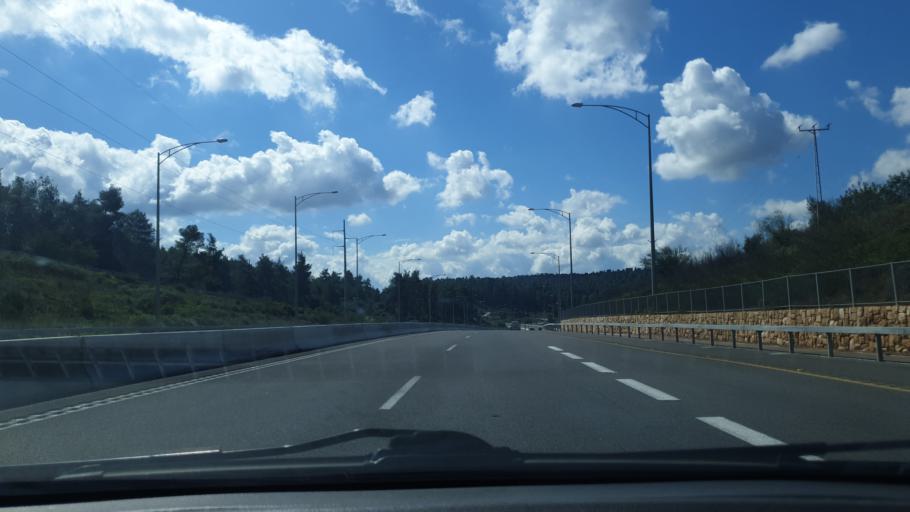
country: IL
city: Mevo horon
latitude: 31.8049
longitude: 35.0170
